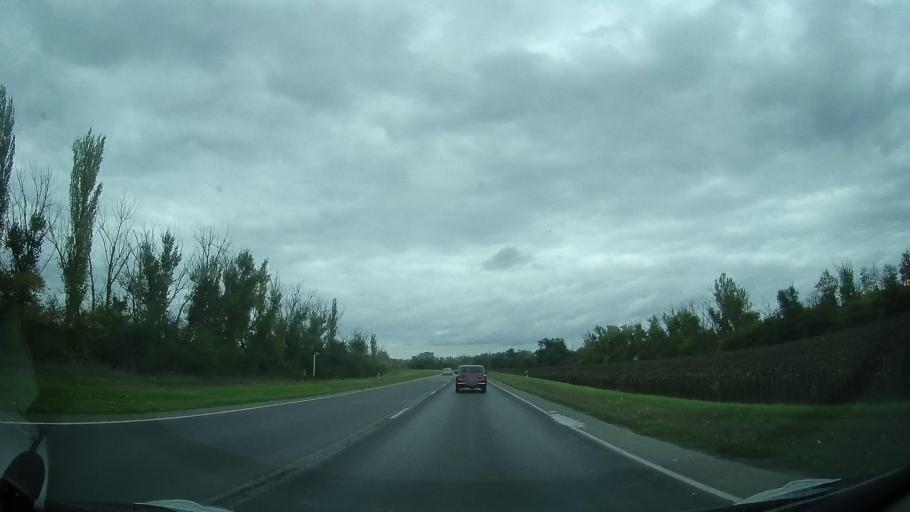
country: RU
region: Rostov
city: Yegorlykskaya
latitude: 46.5414
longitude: 40.7737
